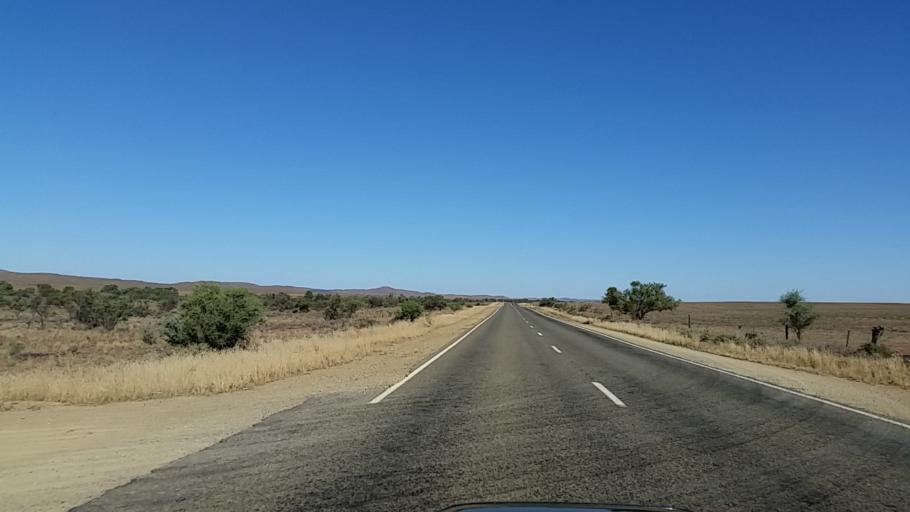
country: AU
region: South Australia
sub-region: Flinders Ranges
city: Quorn
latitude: -32.3989
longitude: 138.5132
